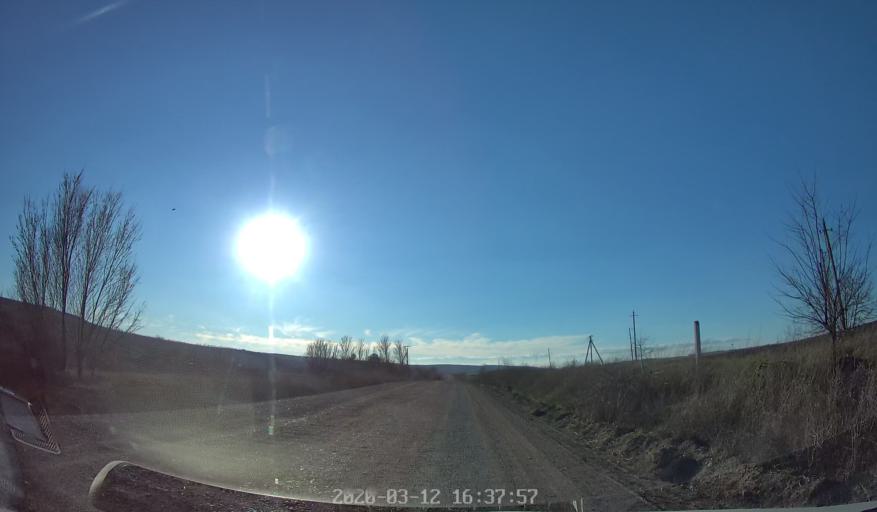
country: MD
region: Anenii Noi
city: Anenii Noi
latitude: 46.8155
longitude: 29.1840
